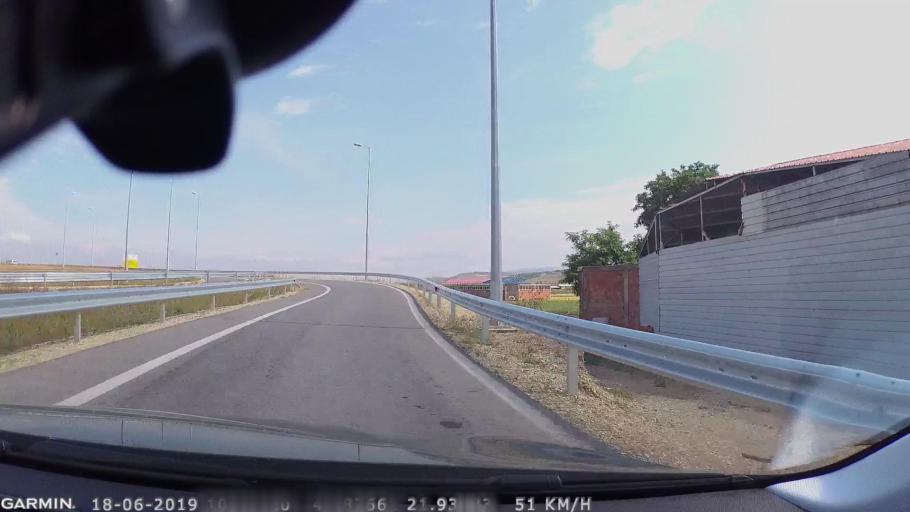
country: MK
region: Sveti Nikole
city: Sveti Nikole
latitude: 41.8766
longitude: 21.9399
